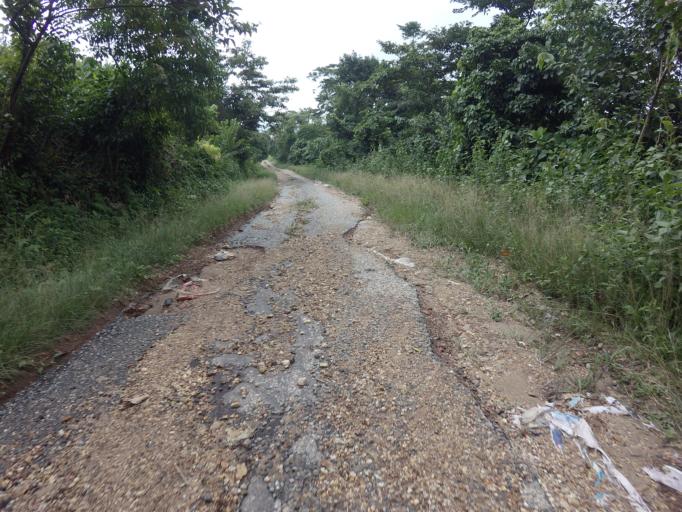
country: GH
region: Volta
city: Kpandu
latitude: 6.8414
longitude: 0.4331
